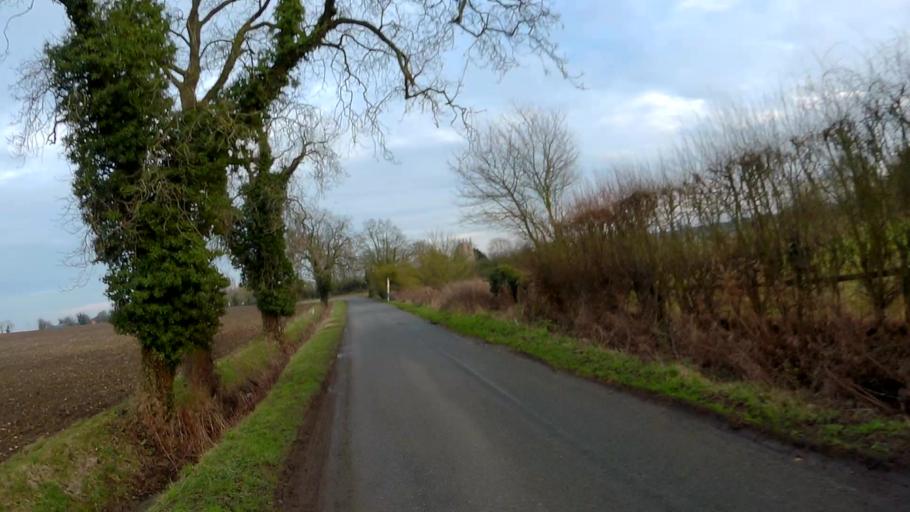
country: GB
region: England
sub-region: Lincolnshire
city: Bourne
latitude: 52.8311
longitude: -0.4170
